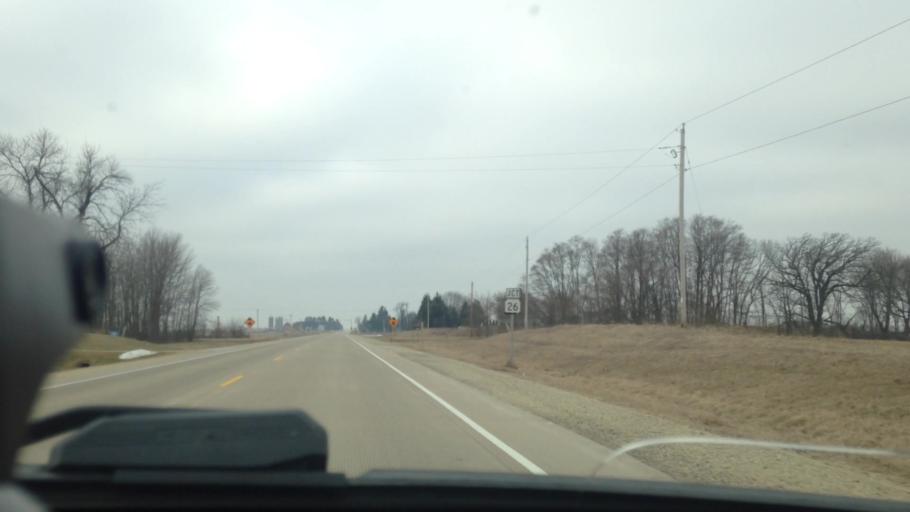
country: US
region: Wisconsin
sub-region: Dodge County
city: Juneau
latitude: 43.4735
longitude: -88.6986
